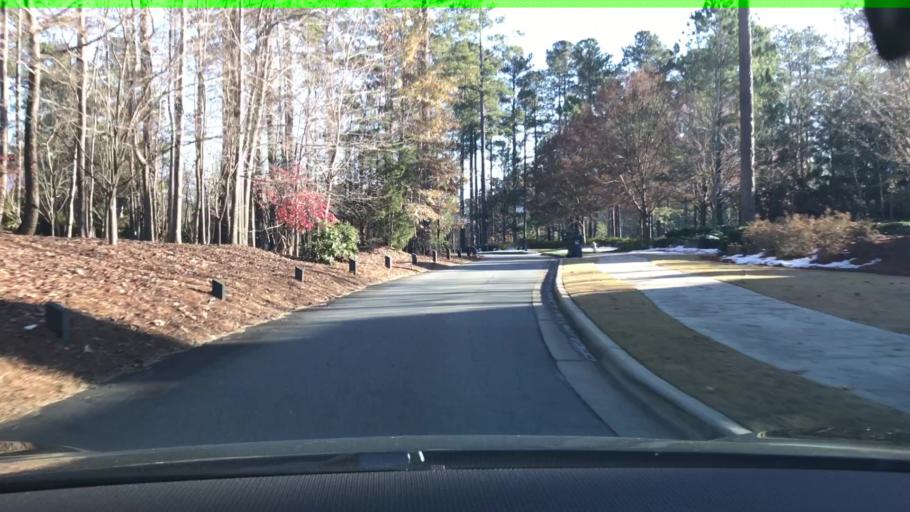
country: US
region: Georgia
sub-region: Gwinnett County
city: Suwanee
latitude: 34.0731
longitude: -84.0976
